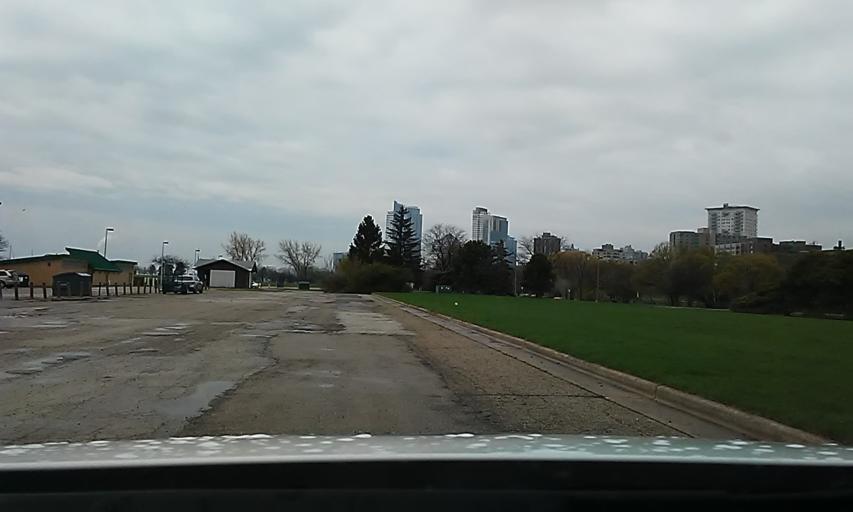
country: US
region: Wisconsin
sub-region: Milwaukee County
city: Milwaukee
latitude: 43.0504
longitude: -87.8878
